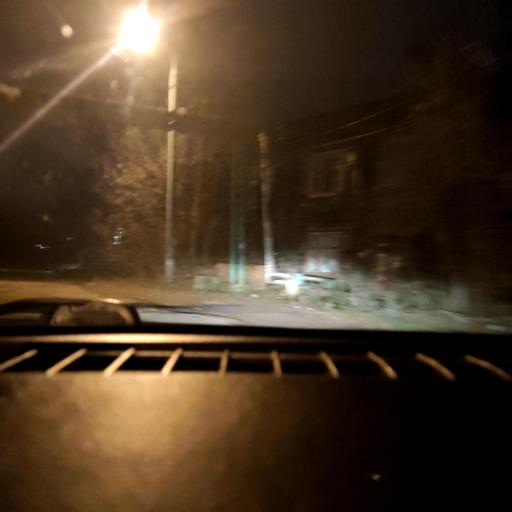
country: RU
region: Perm
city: Perm
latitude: 57.9922
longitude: 56.2262
